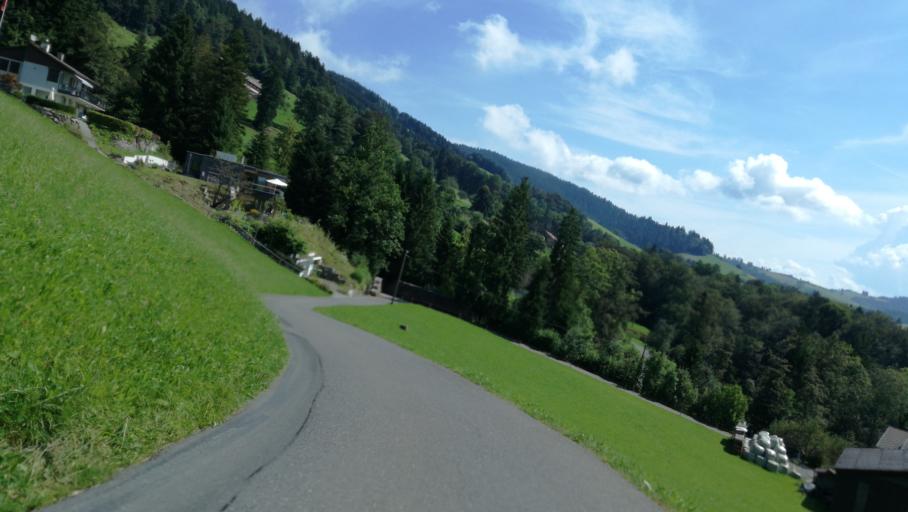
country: CH
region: Zug
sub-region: Zug
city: Unterageri
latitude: 47.1436
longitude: 8.6065
